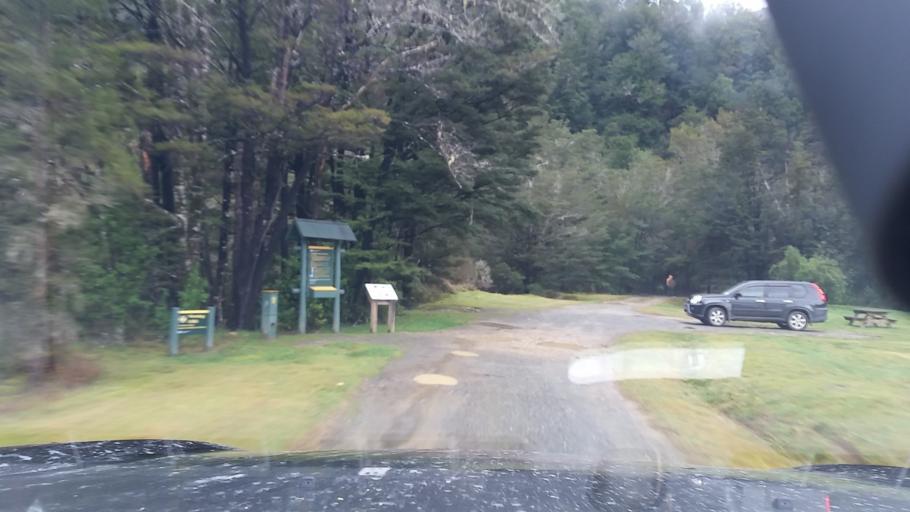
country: NZ
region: Nelson
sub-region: Nelson City
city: Nelson
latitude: -41.3759
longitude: 173.5936
